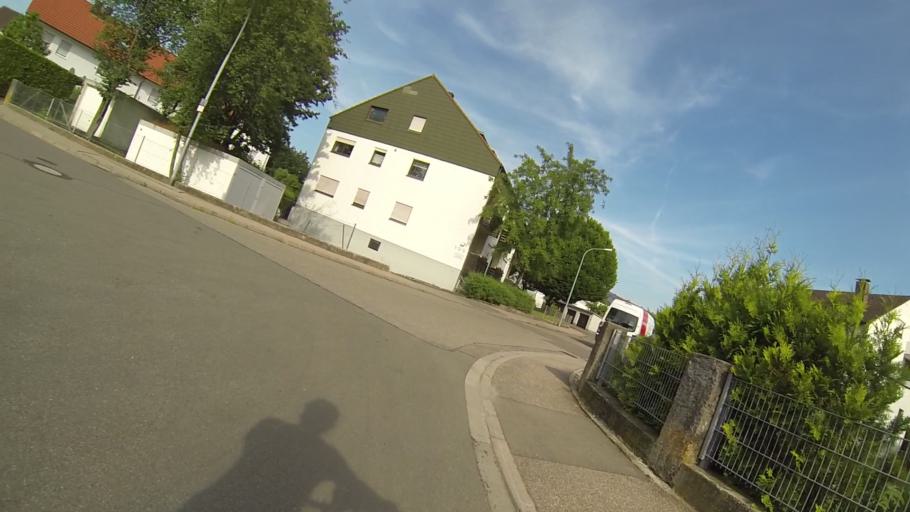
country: DE
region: Bavaria
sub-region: Swabia
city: Senden
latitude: 48.3240
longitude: 10.0295
